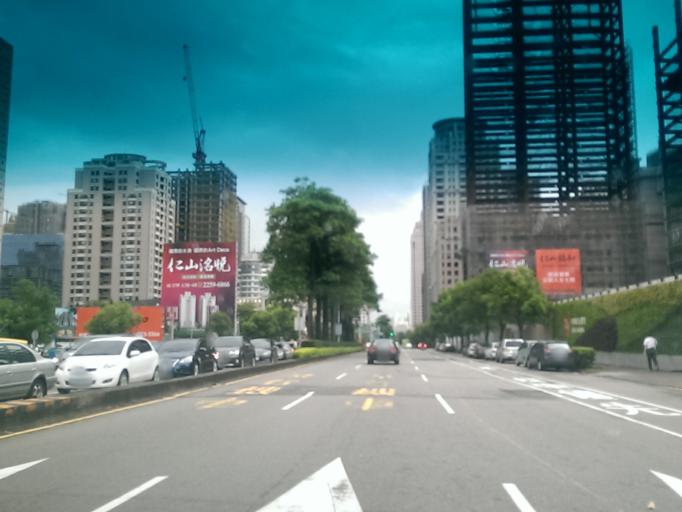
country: TW
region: Taiwan
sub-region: Taichung City
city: Taichung
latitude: 24.1624
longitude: 120.6450
